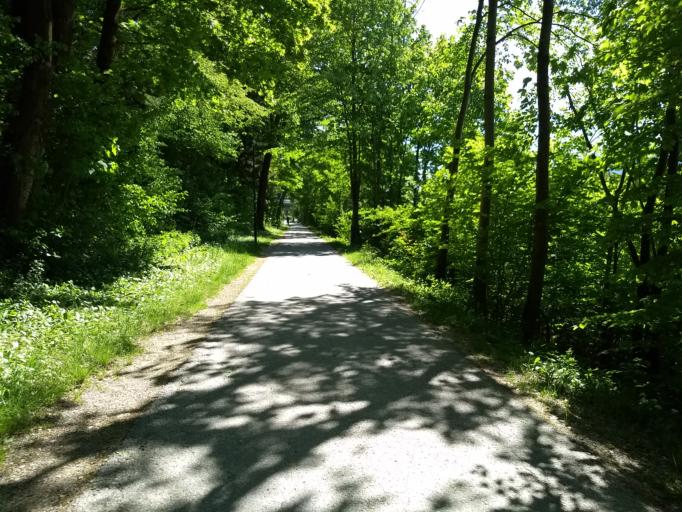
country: AT
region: Salzburg
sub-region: Politischer Bezirk Salzburg-Umgebung
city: Elsbethen
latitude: 47.7728
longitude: 13.0759
